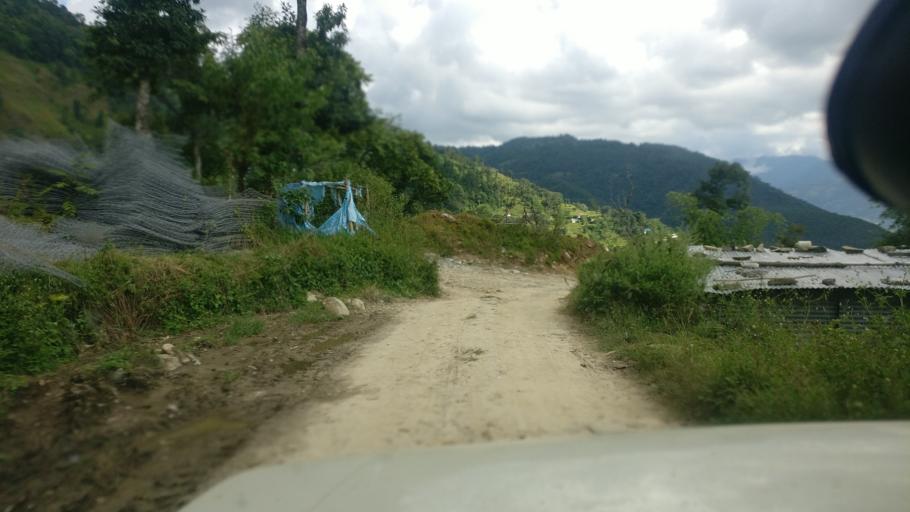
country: NP
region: Western Region
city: Baglung
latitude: 28.2603
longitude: 83.6542
